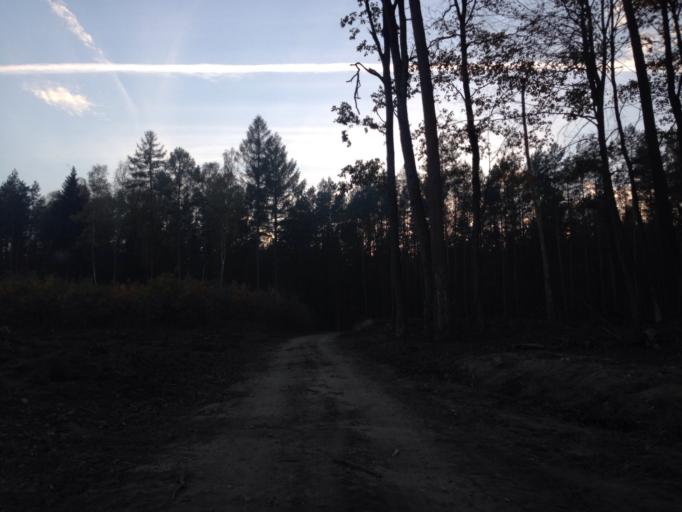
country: PL
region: Kujawsko-Pomorskie
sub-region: Powiat brodnicki
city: Gorzno
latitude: 53.2698
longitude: 19.7156
